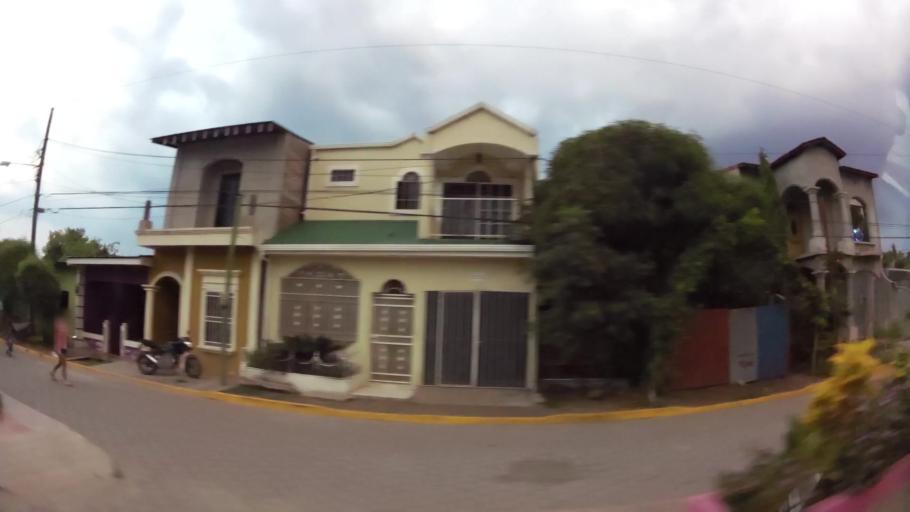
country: NI
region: Matagalpa
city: Ciudad Dario
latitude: 12.8486
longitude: -86.0945
